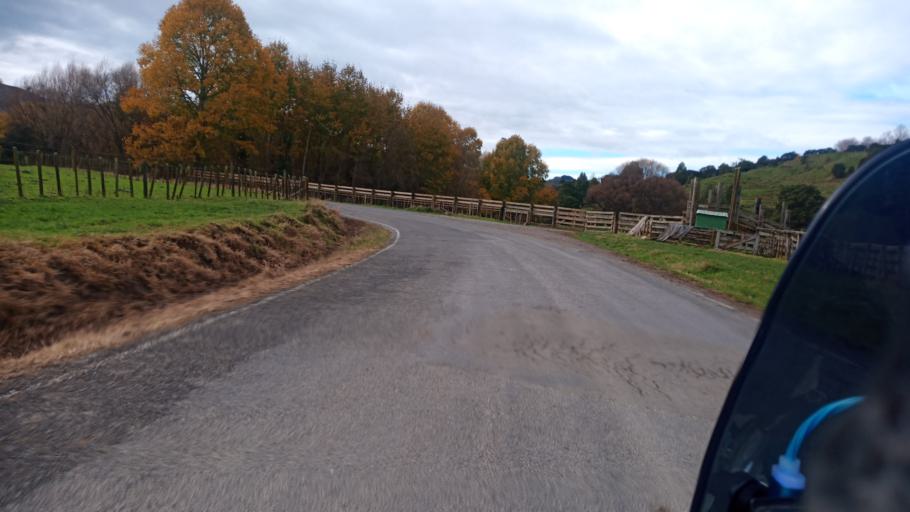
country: NZ
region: Gisborne
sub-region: Gisborne District
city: Gisborne
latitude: -38.4139
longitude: 177.9277
